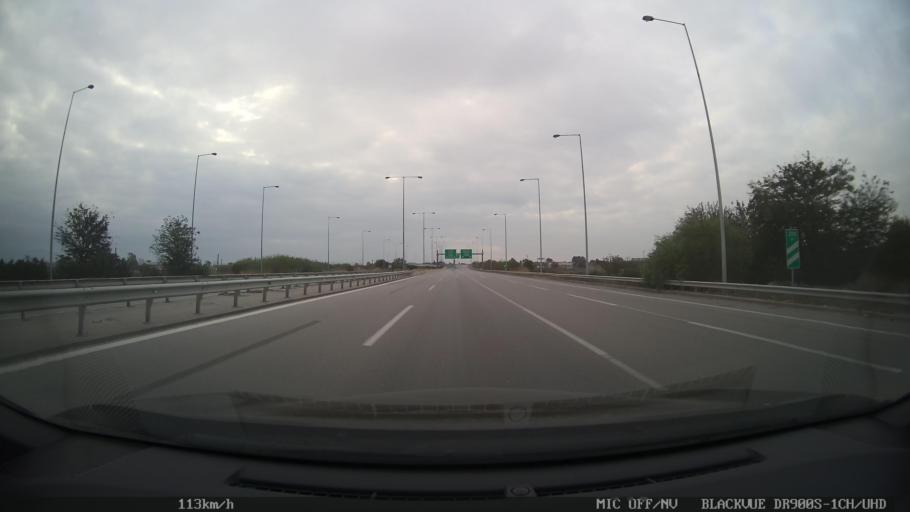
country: GR
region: Central Macedonia
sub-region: Nomos Thessalonikis
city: Kalochori
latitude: 40.6596
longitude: 22.8394
